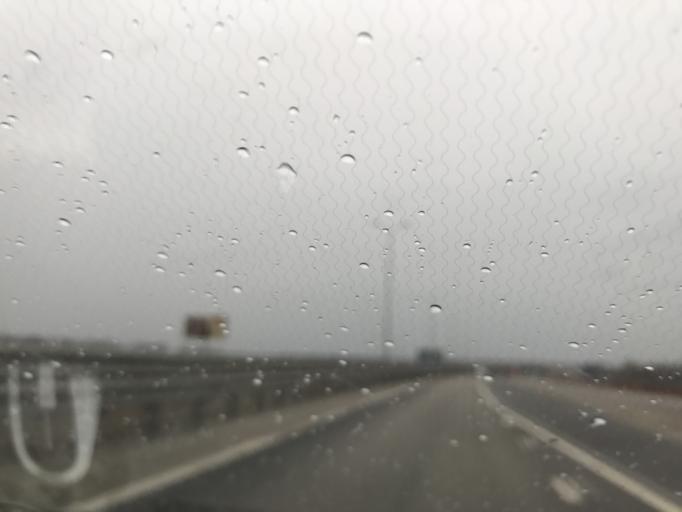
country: RU
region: Krasnodarskiy
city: Pavlovskaya
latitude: 46.1287
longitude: 39.8608
